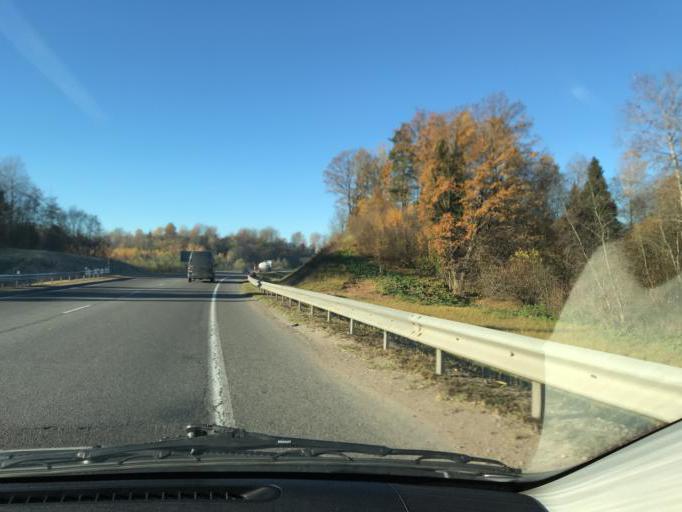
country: BY
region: Vitebsk
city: Vitebsk
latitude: 55.1013
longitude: 30.2809
